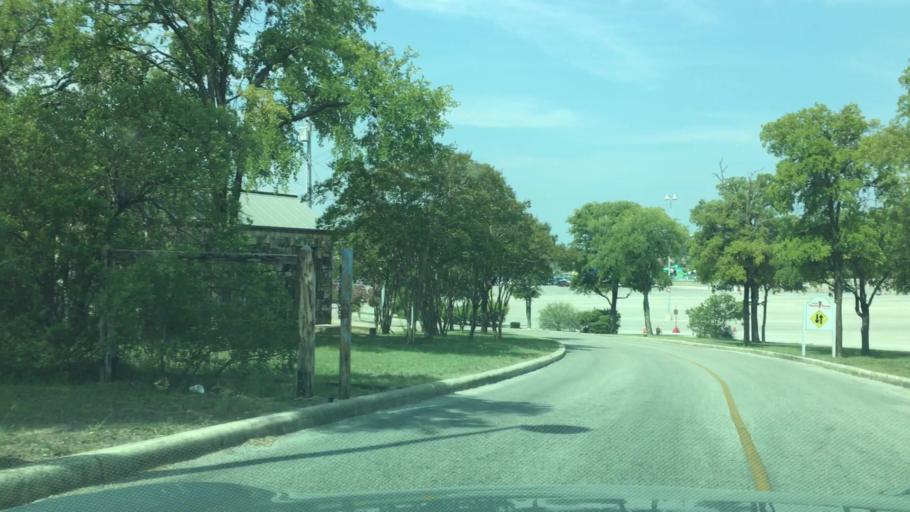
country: US
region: Texas
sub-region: Bexar County
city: Shavano Park
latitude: 29.6023
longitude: -98.6040
